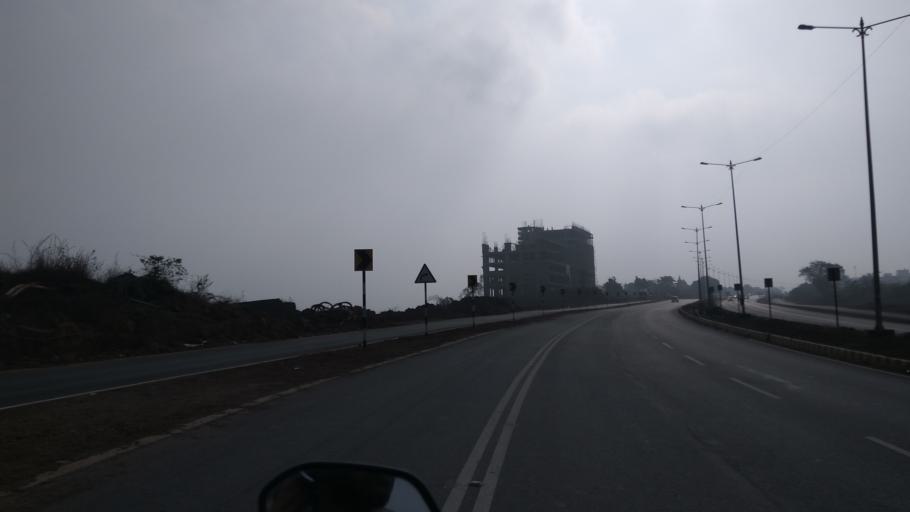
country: IN
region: Goa
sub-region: North Goa
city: Bambolim
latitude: 15.4994
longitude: 73.8741
